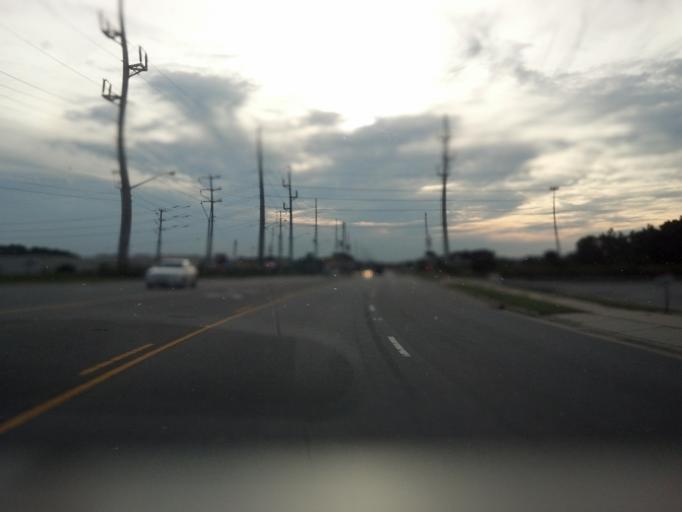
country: US
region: North Carolina
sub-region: Pitt County
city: Winterville
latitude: 35.5486
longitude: -77.3928
